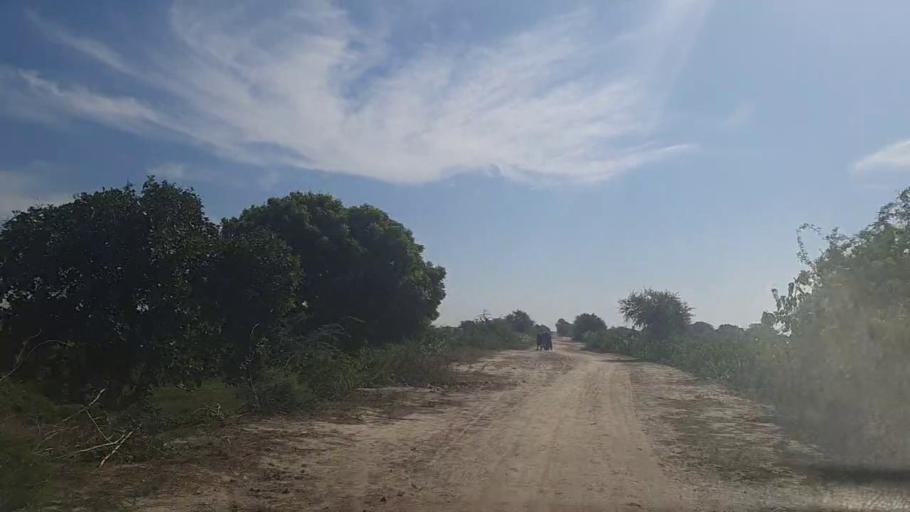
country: PK
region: Sindh
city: Mirpur Batoro
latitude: 24.6559
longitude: 68.1998
